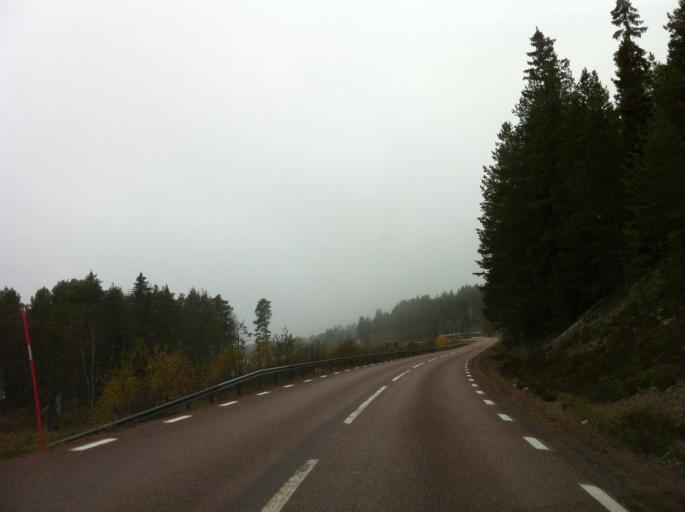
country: NO
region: Hedmark
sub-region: Trysil
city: Innbygda
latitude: 61.8517
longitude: 12.7509
